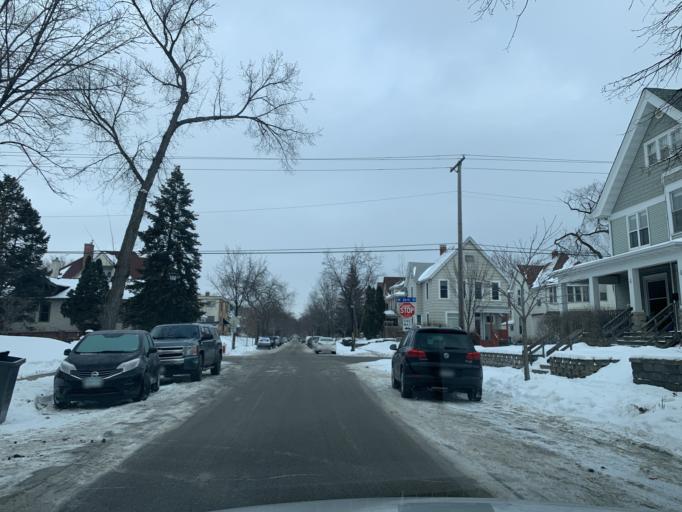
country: US
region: Minnesota
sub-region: Hennepin County
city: Minneapolis
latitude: 44.9552
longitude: -93.2918
